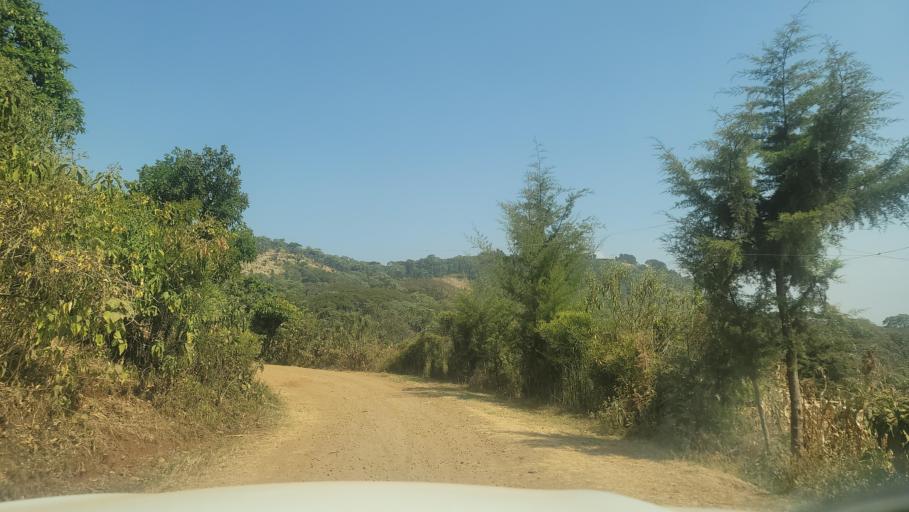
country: ET
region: Oromiya
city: Agaro
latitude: 7.8455
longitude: 36.5388
